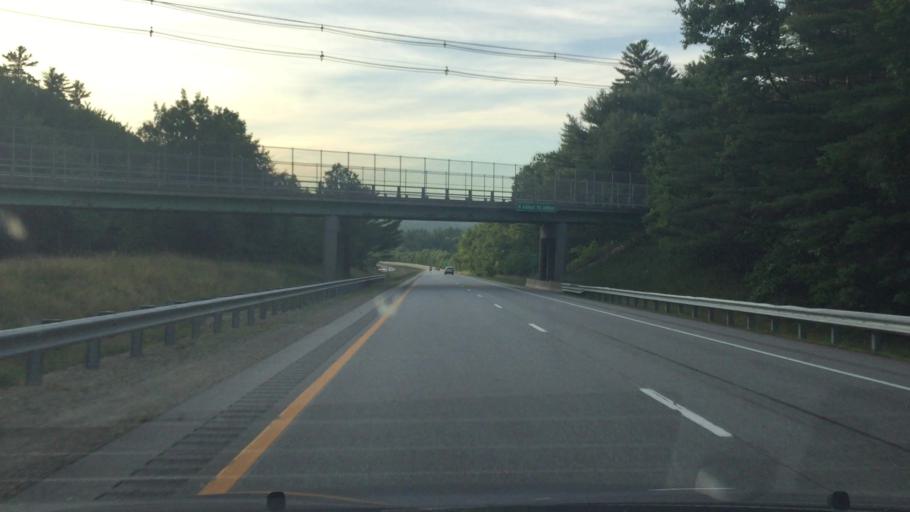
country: US
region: New Hampshire
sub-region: Grafton County
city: Plymouth
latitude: 43.7433
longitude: -71.6618
